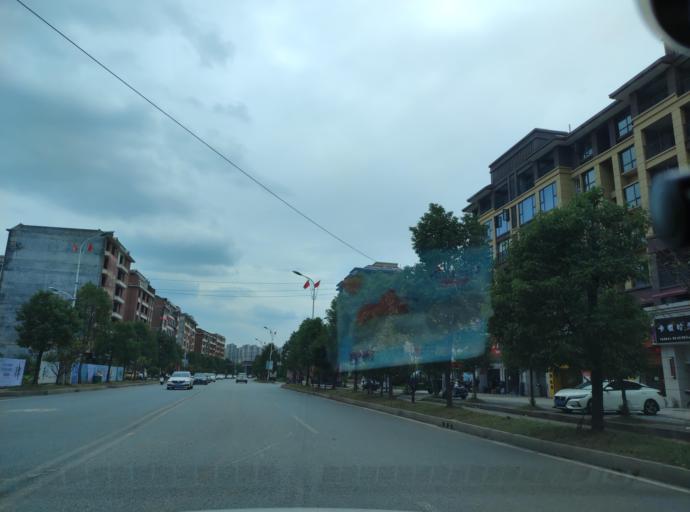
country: CN
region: Jiangxi Sheng
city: Pingxiang
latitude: 27.6757
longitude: 113.9056
